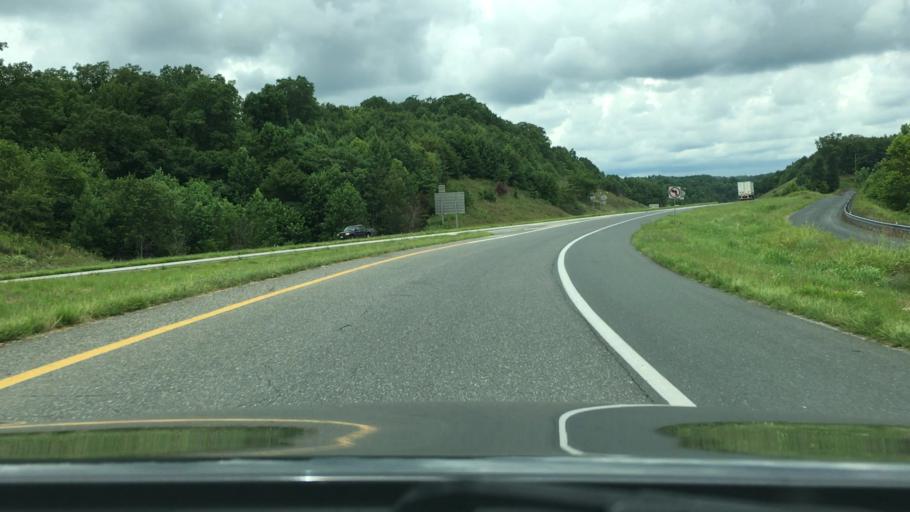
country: US
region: Virginia
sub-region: Amherst County
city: Madison Heights
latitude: 37.4112
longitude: -79.0818
